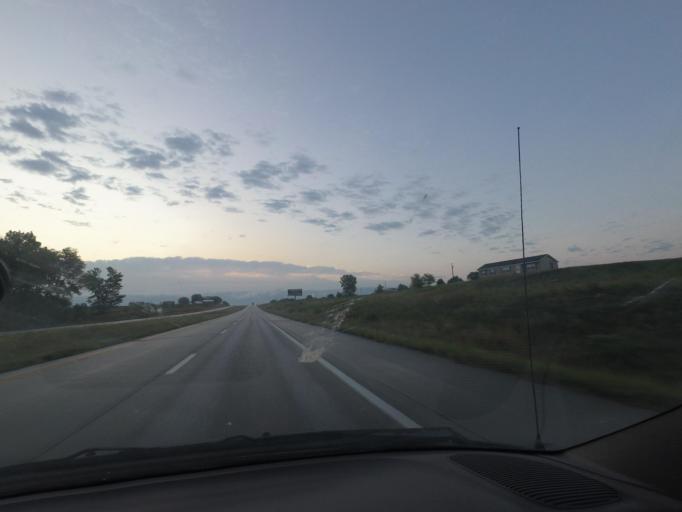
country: US
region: Missouri
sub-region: Macon County
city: Macon
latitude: 39.7554
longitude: -92.5405
